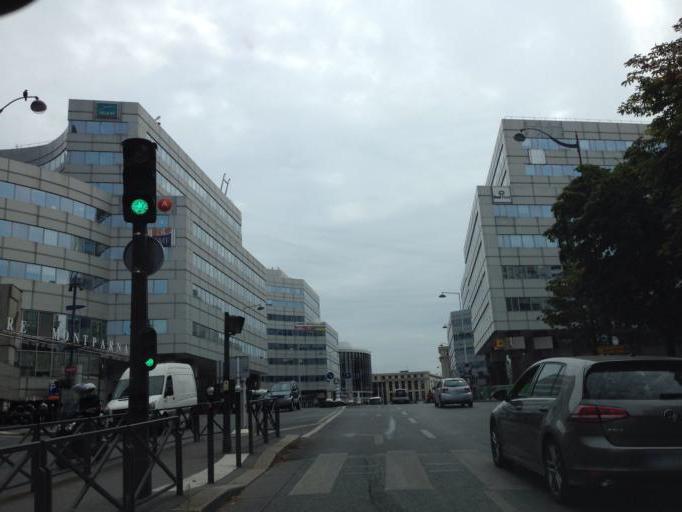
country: FR
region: Ile-de-France
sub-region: Departement des Hauts-de-Seine
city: Montrouge
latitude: 48.8393
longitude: 2.3162
